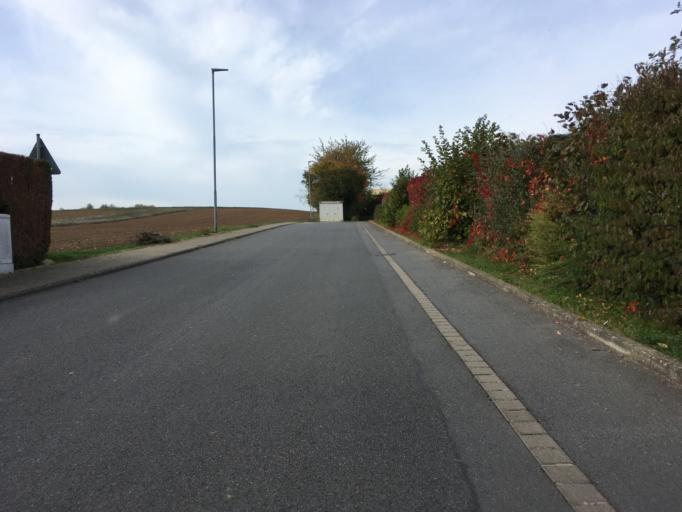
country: DE
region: Baden-Wuerttemberg
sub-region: Karlsruhe Region
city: Rosenberg
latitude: 49.4607
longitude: 9.4747
